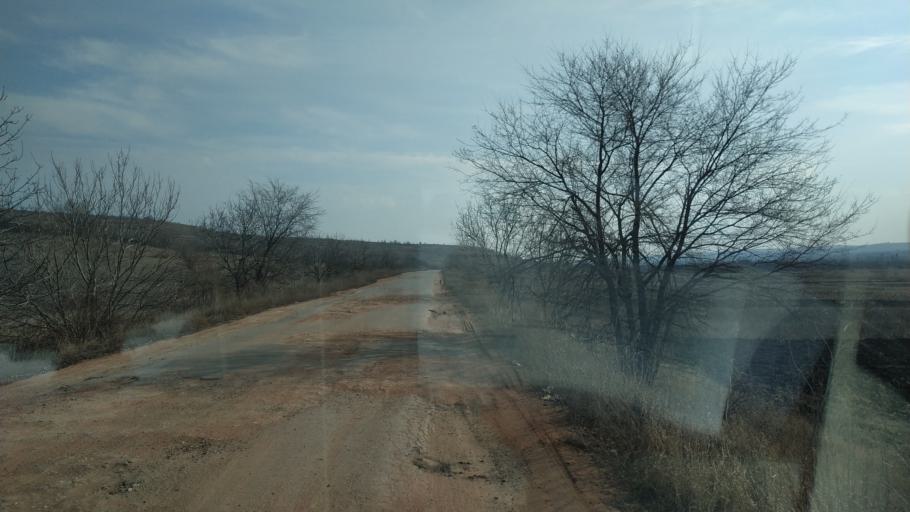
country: MD
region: Chisinau
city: Singera
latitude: 46.9242
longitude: 29.0856
